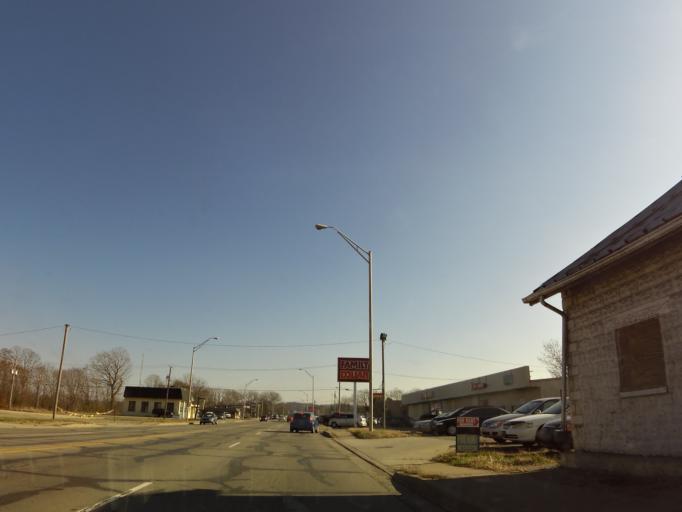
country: US
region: Indiana
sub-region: Fayette County
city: Connersville
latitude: 39.6400
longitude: -85.1354
